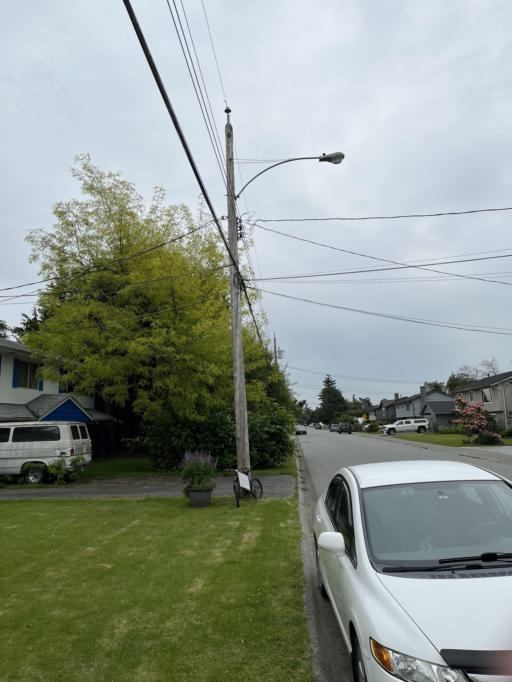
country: CA
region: British Columbia
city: Ladner
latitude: 49.0855
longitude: -123.0751
